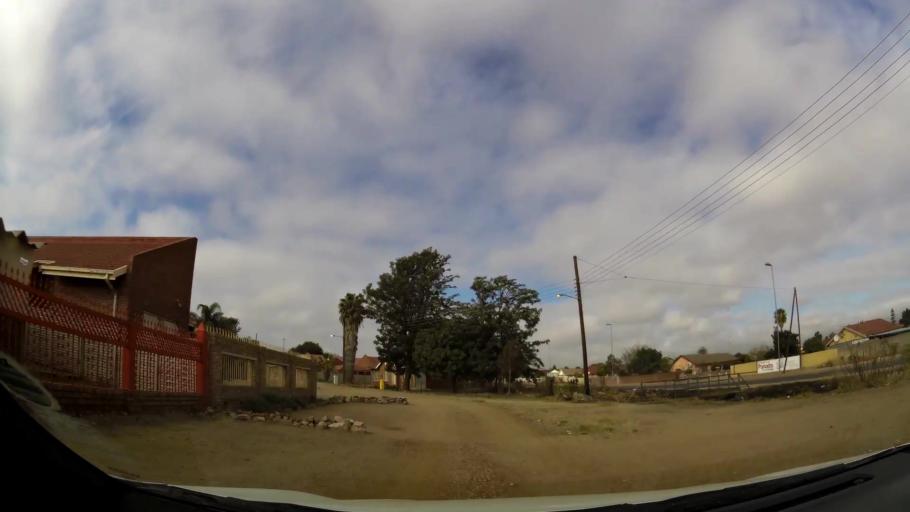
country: ZA
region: Limpopo
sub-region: Capricorn District Municipality
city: Polokwane
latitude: -23.8469
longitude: 29.3794
